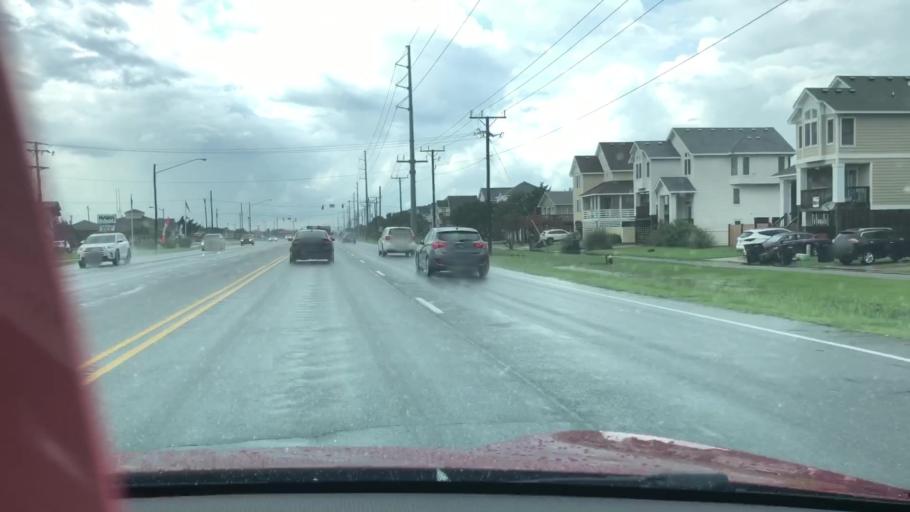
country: US
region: North Carolina
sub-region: Dare County
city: Kill Devil Hills
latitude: 36.0290
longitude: -75.6695
